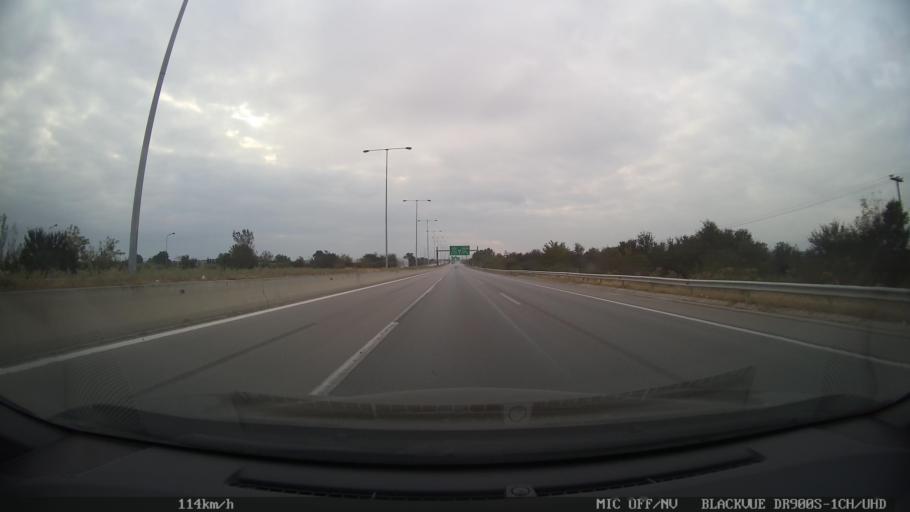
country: GR
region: Central Macedonia
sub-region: Nomos Thessalonikis
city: Nea Magnisia
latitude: 40.6640
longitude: 22.8371
